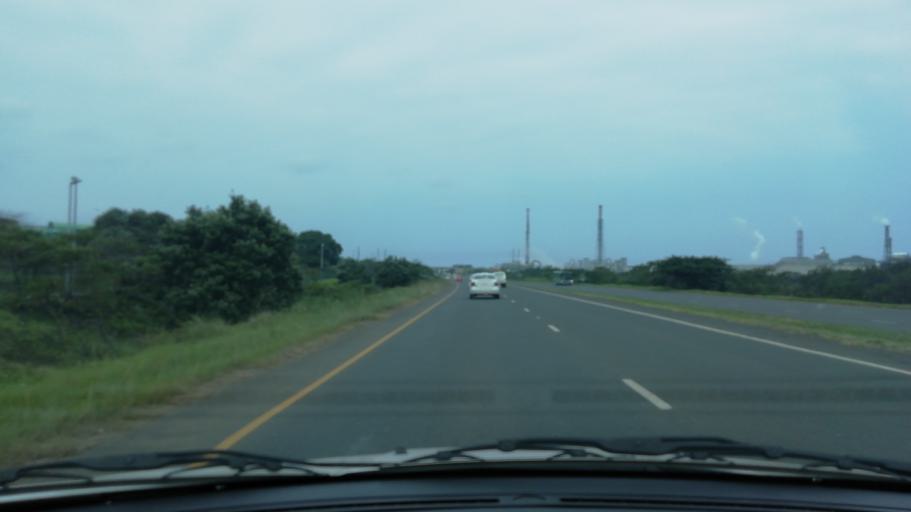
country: ZA
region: KwaZulu-Natal
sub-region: uThungulu District Municipality
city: Richards Bay
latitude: -28.7717
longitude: 32.0260
